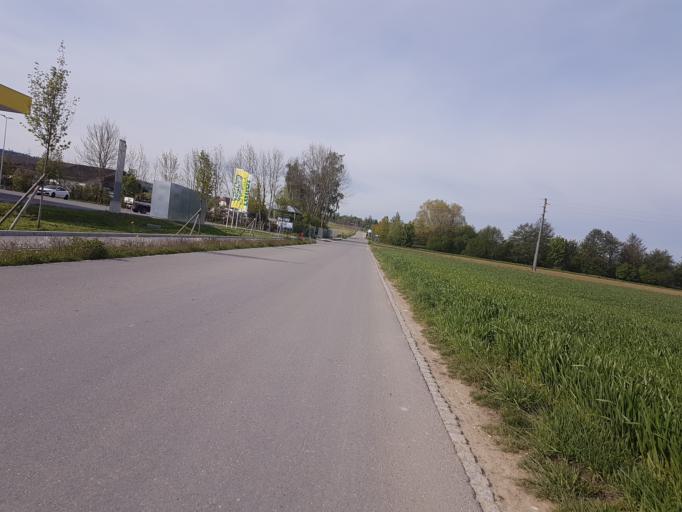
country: CH
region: Bern
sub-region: Biel/Bienne District
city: Bellmund
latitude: 47.1096
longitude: 7.2237
